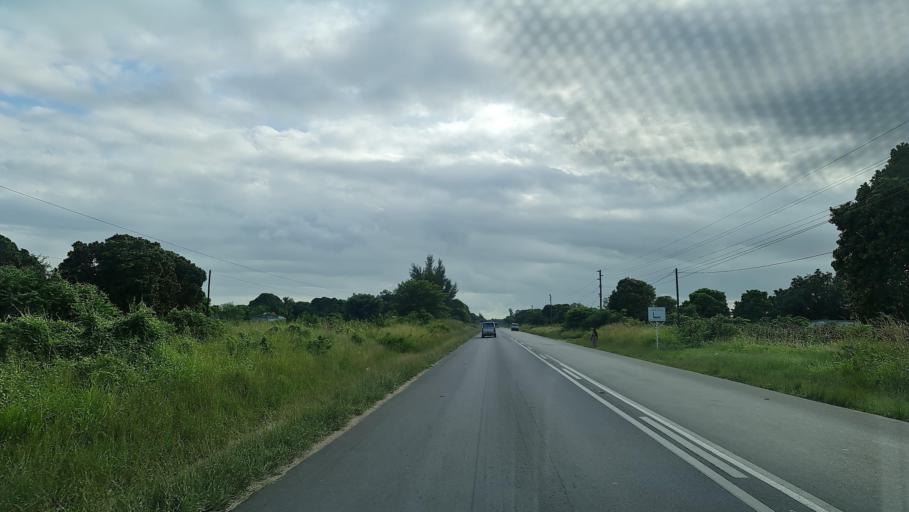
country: MZ
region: Maputo
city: Manhica
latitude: -25.4170
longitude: 32.7341
